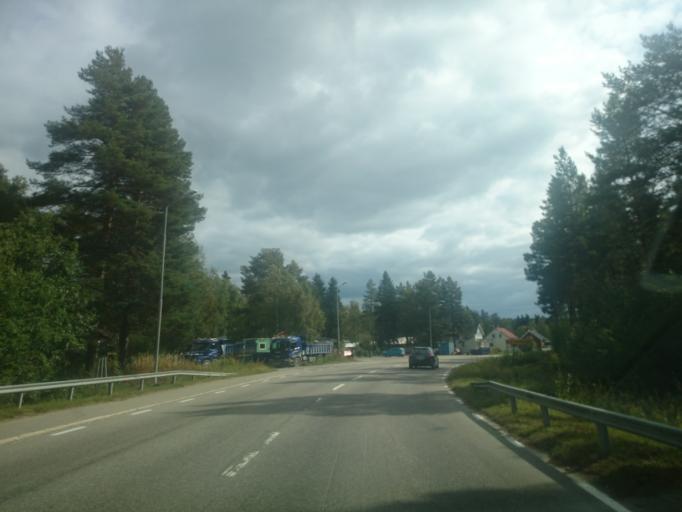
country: SE
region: Jaemtland
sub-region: Harjedalens Kommun
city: Sveg
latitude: 62.4261
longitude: 13.5293
